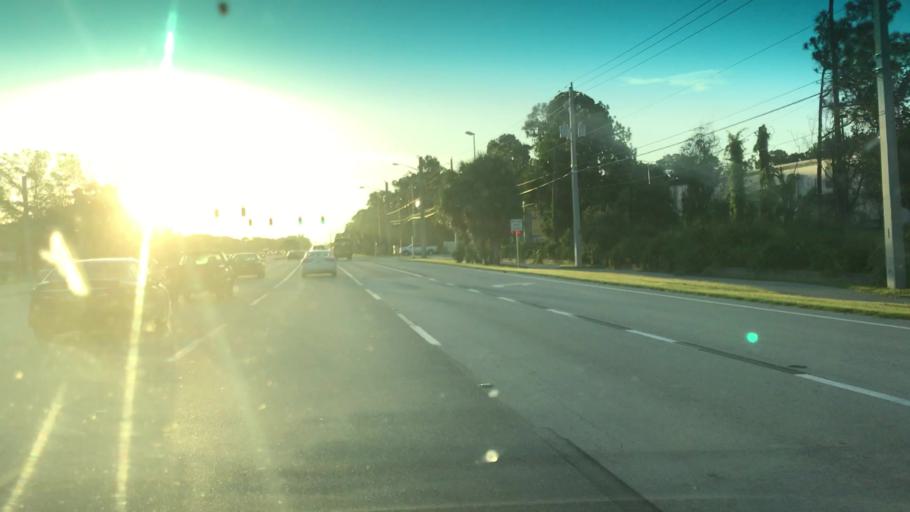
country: US
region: Florida
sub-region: Lee County
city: Villas
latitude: 26.5462
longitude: -81.8692
